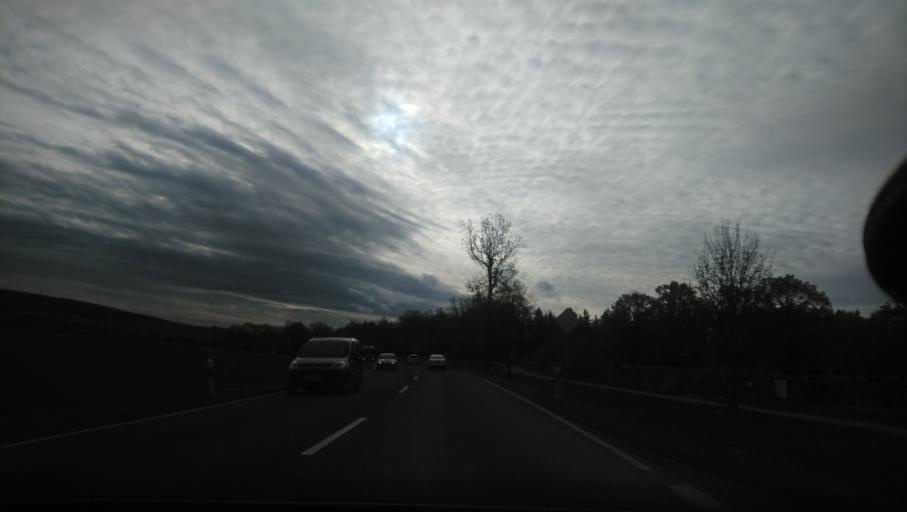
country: DE
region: Saxony
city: Zwonitz
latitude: 50.6556
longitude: 12.8099
